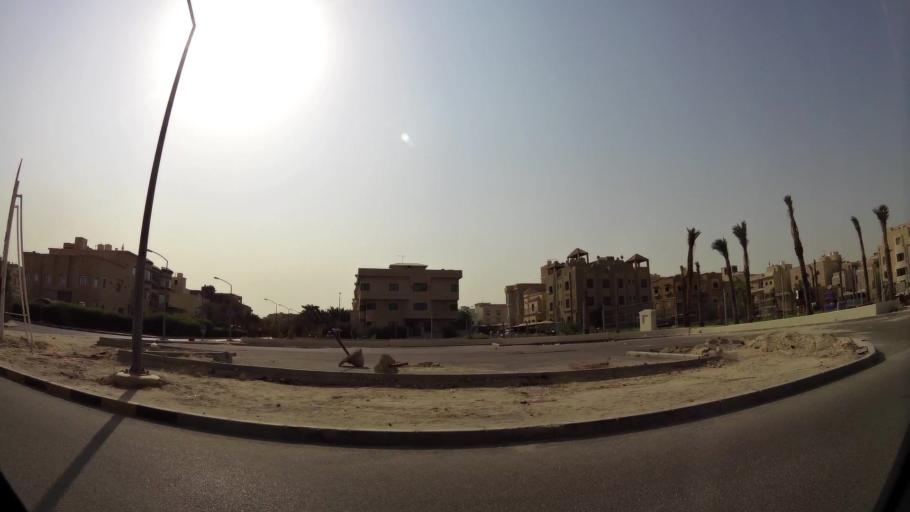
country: KW
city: Bayan
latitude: 29.2813
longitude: 48.0444
